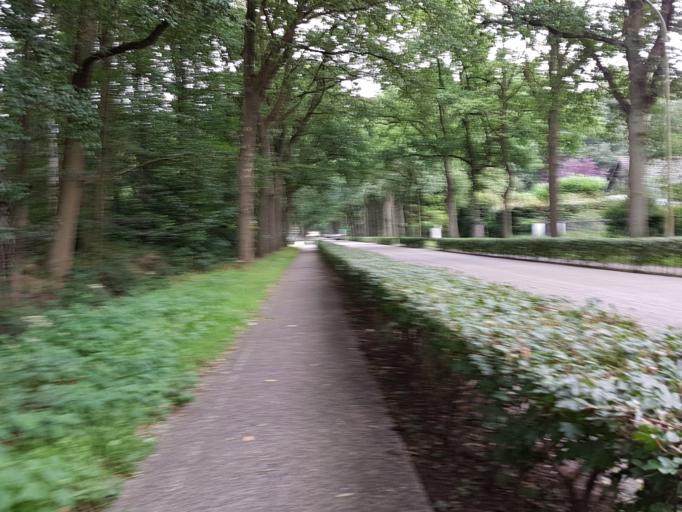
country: BE
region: Flanders
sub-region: Provincie Antwerpen
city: Kalmthout
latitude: 51.3683
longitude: 4.4439
